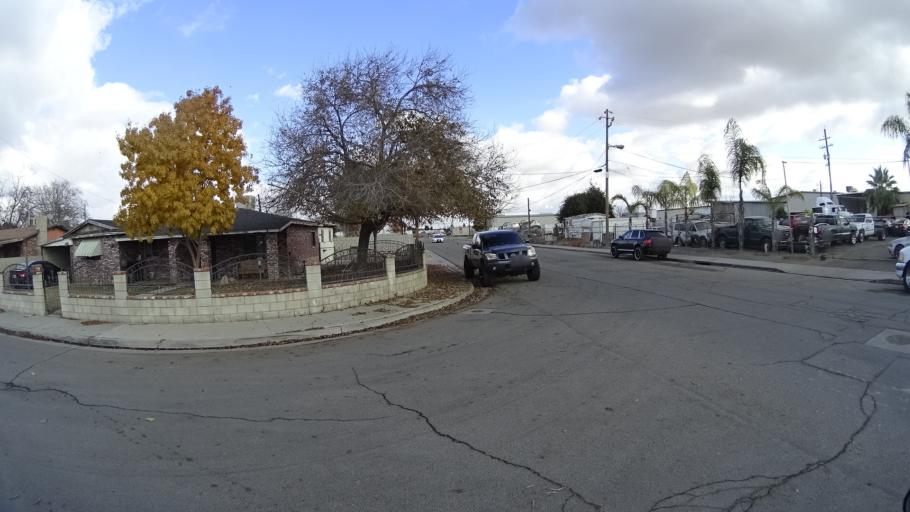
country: US
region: California
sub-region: Kern County
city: Bakersfield
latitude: 35.3579
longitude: -118.9603
